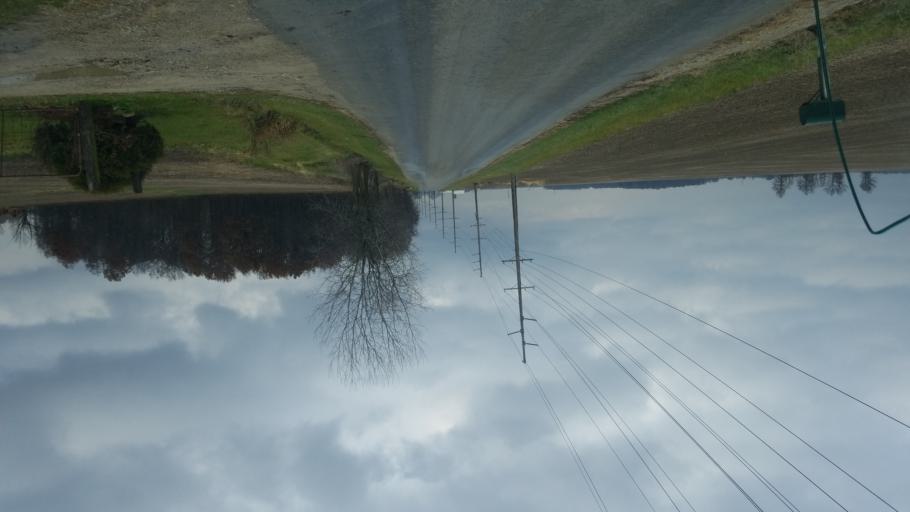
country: US
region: Indiana
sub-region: Jay County
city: Portland
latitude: 40.5122
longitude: -84.9648
